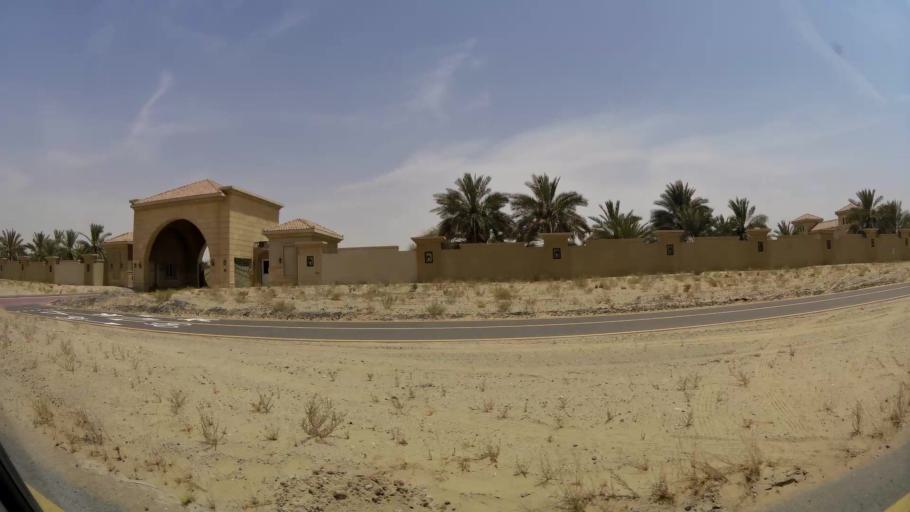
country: AE
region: Ash Shariqah
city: Sharjah
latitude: 25.2351
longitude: 55.4777
